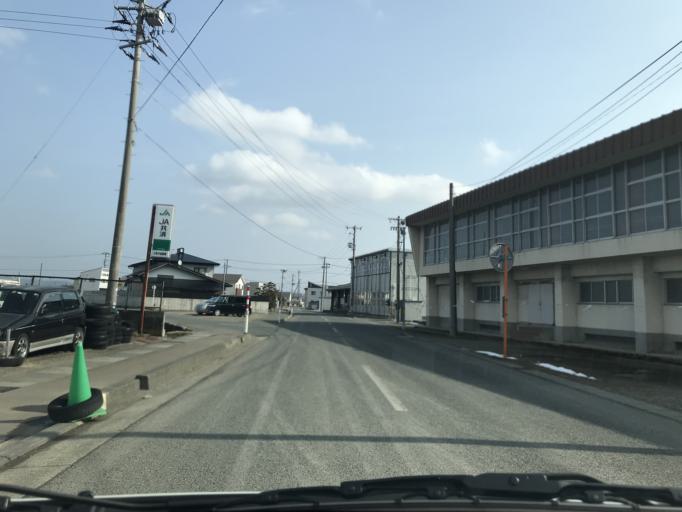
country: JP
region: Iwate
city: Kitakami
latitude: 39.2975
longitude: 141.0760
